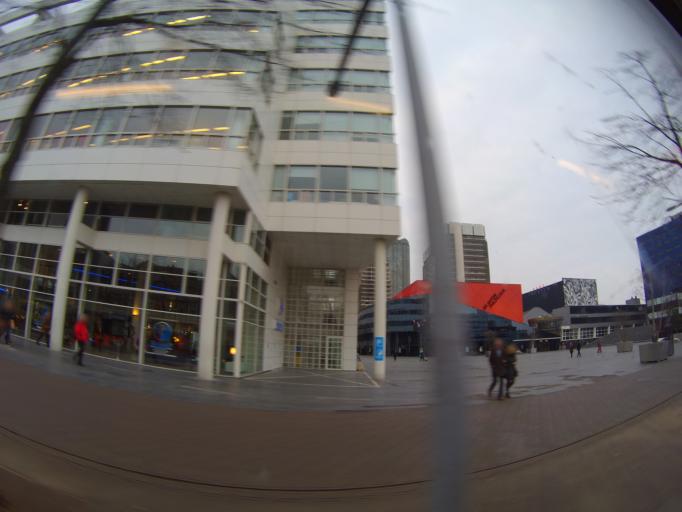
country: NL
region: South Holland
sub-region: Gemeente Den Haag
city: The Hague
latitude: 52.0770
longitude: 4.3164
